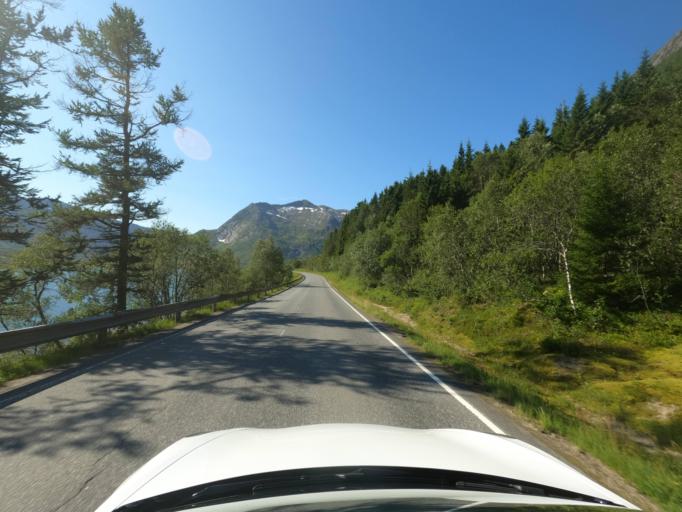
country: NO
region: Nordland
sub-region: Lodingen
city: Lodingen
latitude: 68.5508
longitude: 15.7482
